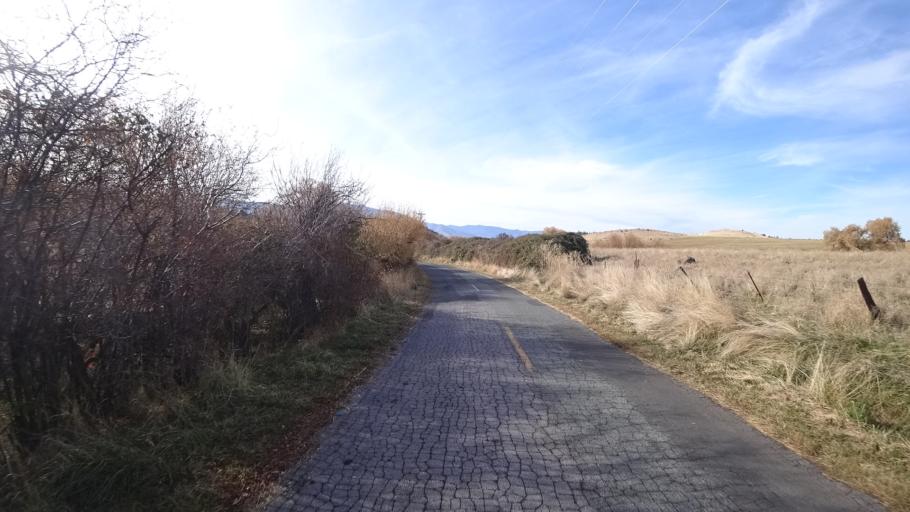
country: US
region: California
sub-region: Siskiyou County
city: Weed
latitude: 41.4651
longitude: -122.3915
